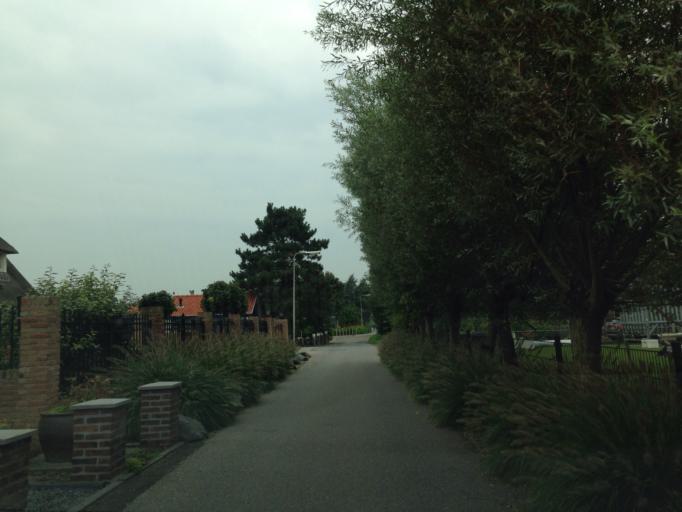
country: NL
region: South Holland
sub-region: Gemeente Westland
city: Maasdijk
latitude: 51.9744
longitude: 4.2096
